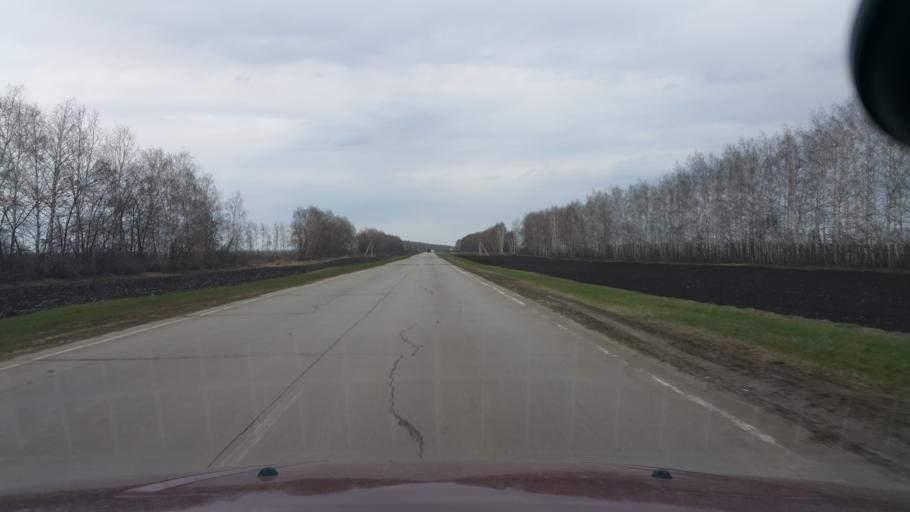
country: RU
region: Tambov
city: Bokino
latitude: 52.5668
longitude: 41.3771
